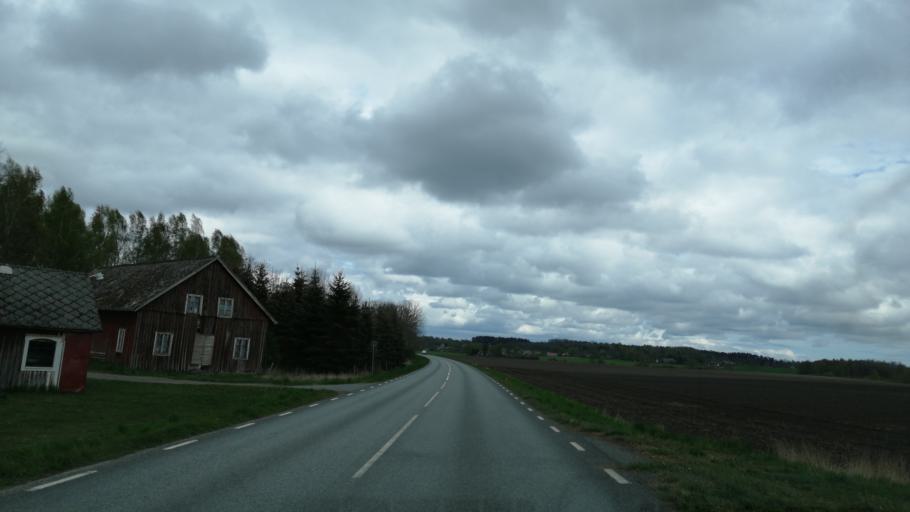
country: SE
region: Skane
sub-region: Kristianstads Kommun
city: Fjalkinge
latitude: 56.0680
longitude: 14.3358
